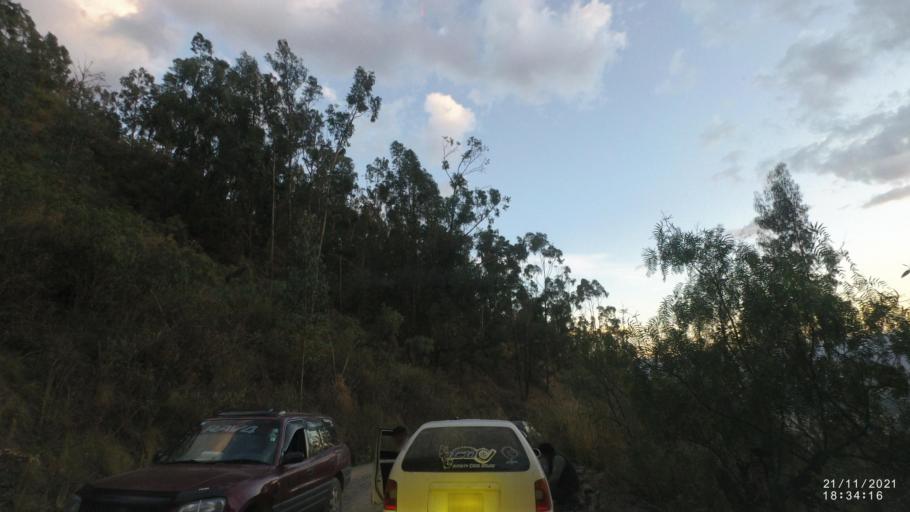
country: BO
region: Cochabamba
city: Cochabamba
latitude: -17.3099
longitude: -66.2200
